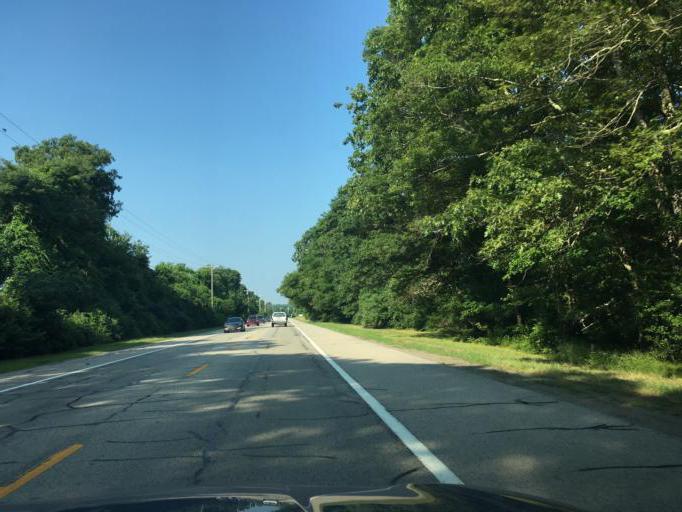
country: US
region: Rhode Island
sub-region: Washington County
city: Exeter
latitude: 41.5526
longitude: -71.5250
